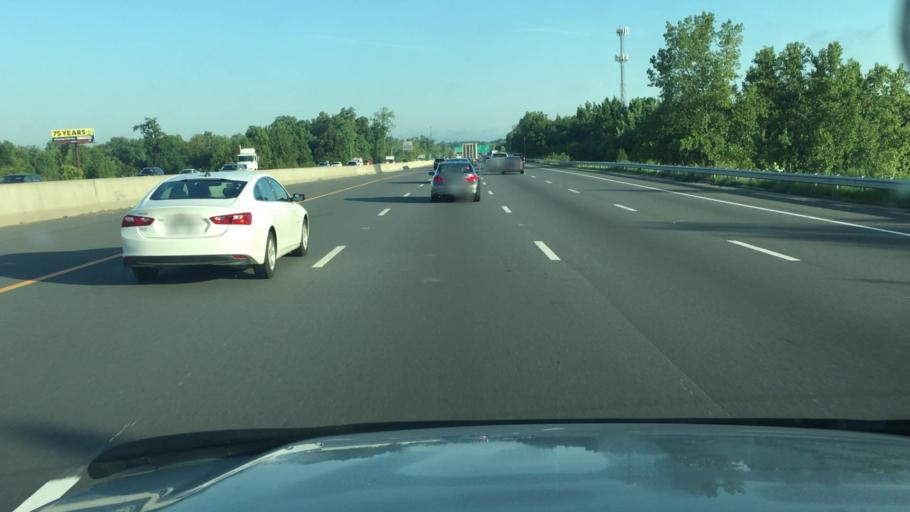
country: US
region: North Carolina
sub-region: Mecklenburg County
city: Pineville
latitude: 35.1090
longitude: -80.8952
